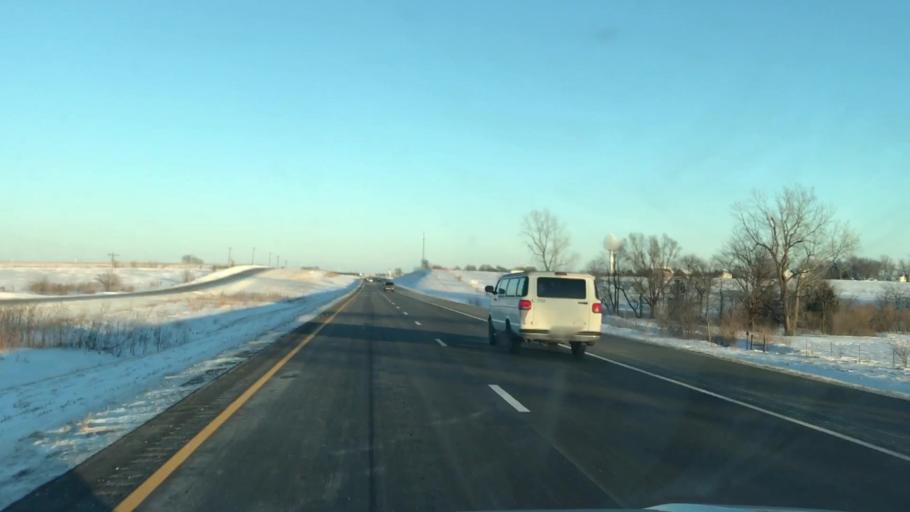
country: US
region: Missouri
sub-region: Clinton County
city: Gower
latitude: 39.7620
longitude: -94.5146
